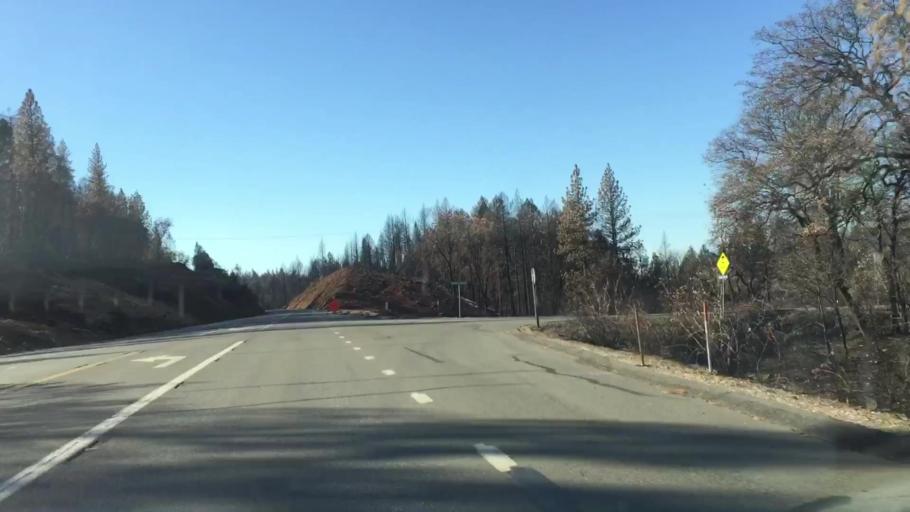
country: US
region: California
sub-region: Butte County
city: Magalia
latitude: 39.7256
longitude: -121.5027
